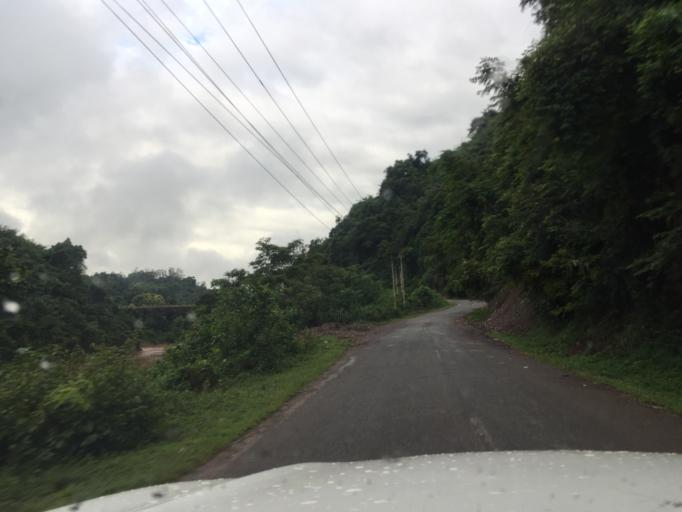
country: LA
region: Oudomxai
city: Muang La
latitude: 20.8670
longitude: 102.1251
